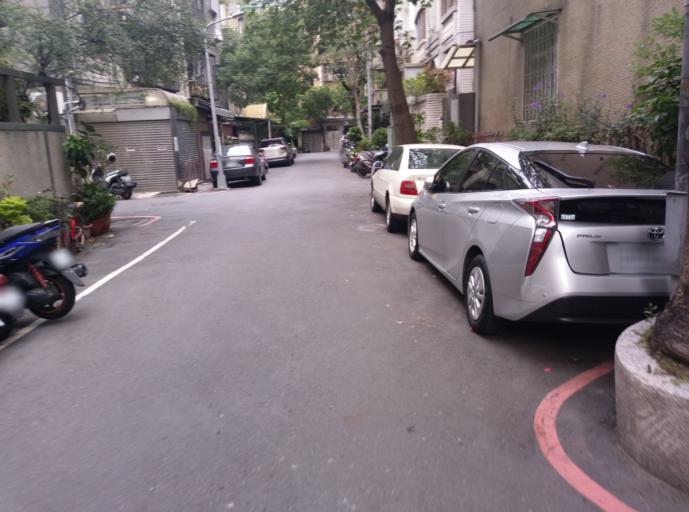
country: TW
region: Taipei
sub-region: Taipei
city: Banqiao
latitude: 25.0134
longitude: 121.4548
